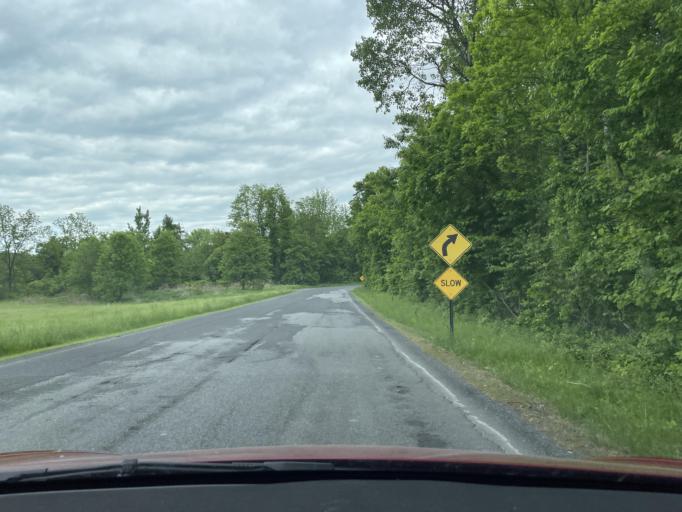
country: US
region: New York
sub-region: Ulster County
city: Saugerties
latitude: 42.0876
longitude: -73.9577
